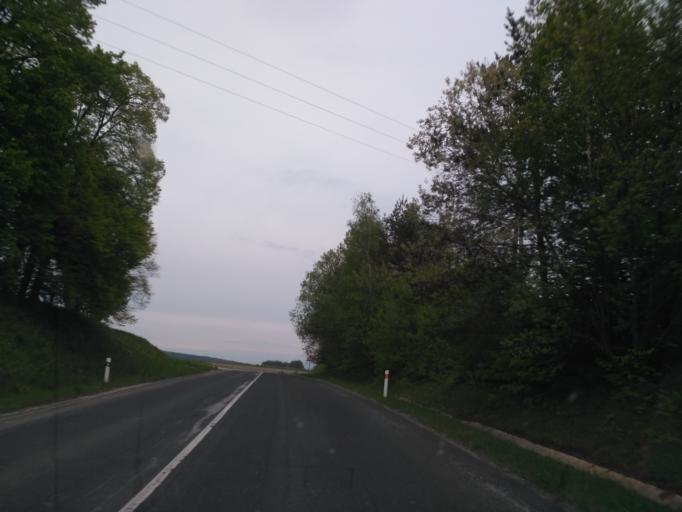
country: SK
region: Kosicky
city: Moldava nad Bodvou
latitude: 48.6811
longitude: 21.0751
